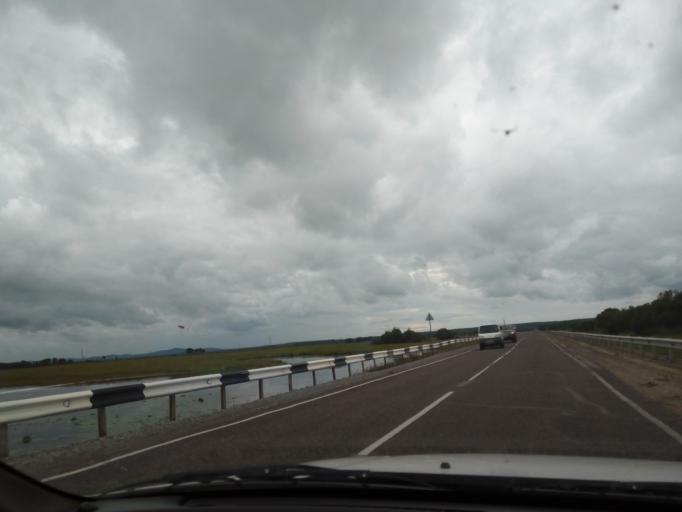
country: RU
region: Primorskiy
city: Dal'nerechensk
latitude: 45.9149
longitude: 133.7698
